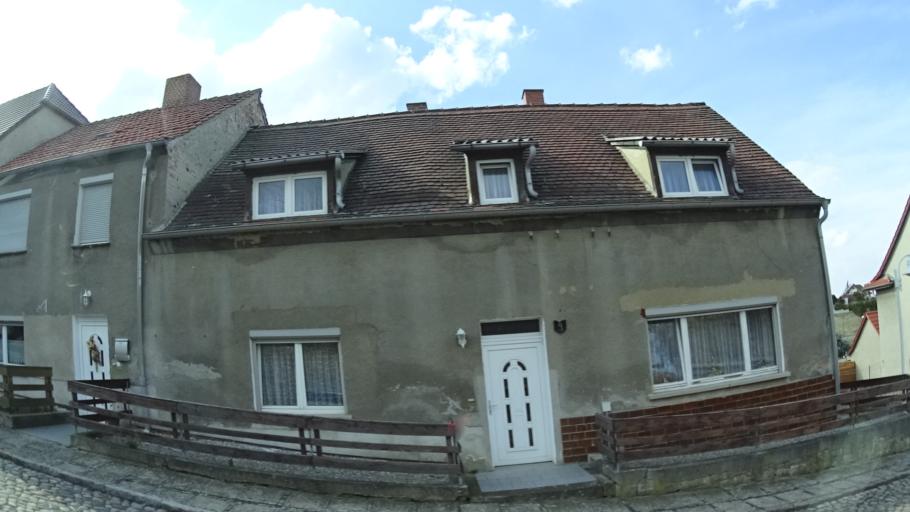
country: DE
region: Saxony-Anhalt
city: Stossen
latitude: 51.1171
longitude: 11.9268
